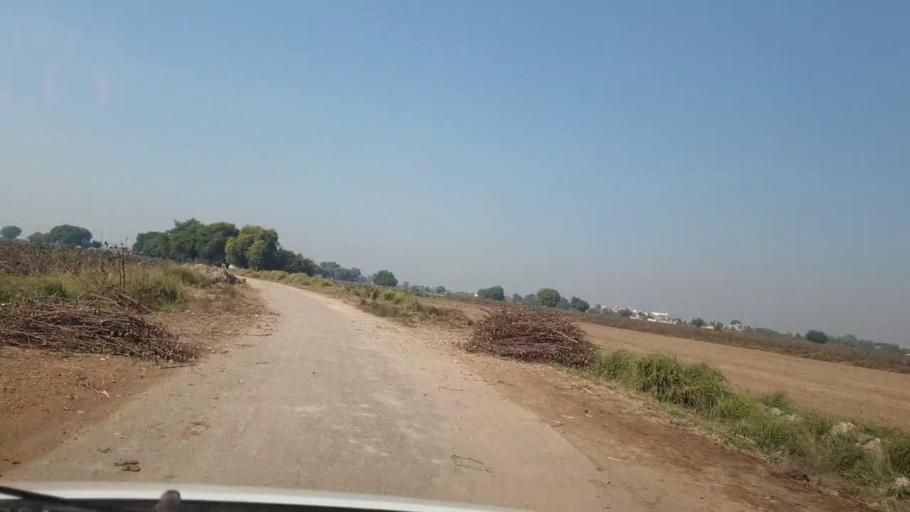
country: PK
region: Sindh
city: Bhan
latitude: 26.6427
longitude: 67.7125
